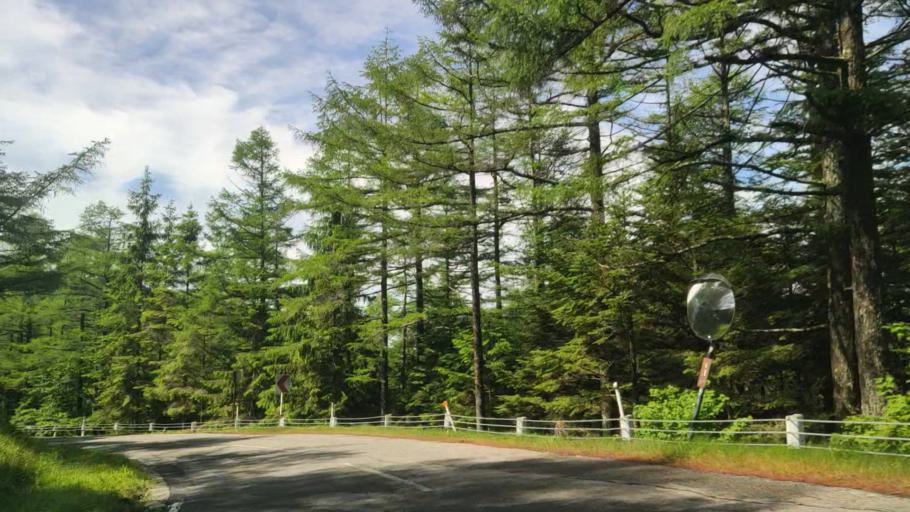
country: JP
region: Nagano
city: Suwa
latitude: 36.0972
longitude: 138.1513
